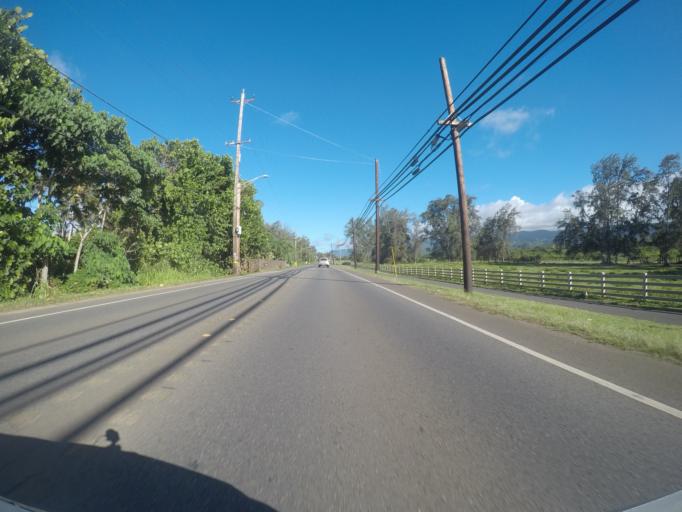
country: US
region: Hawaii
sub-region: Honolulu County
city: Kahuku
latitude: 21.6639
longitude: -157.9360
